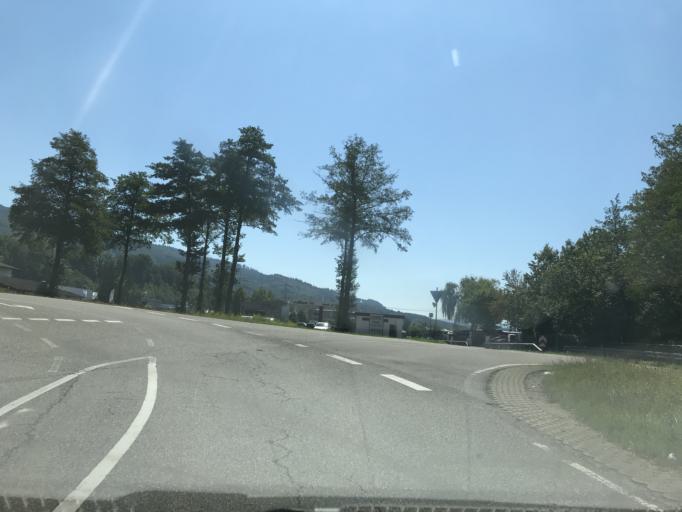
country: DE
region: Baden-Wuerttemberg
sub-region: Freiburg Region
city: Wehr
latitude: 47.6121
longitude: 7.9101
